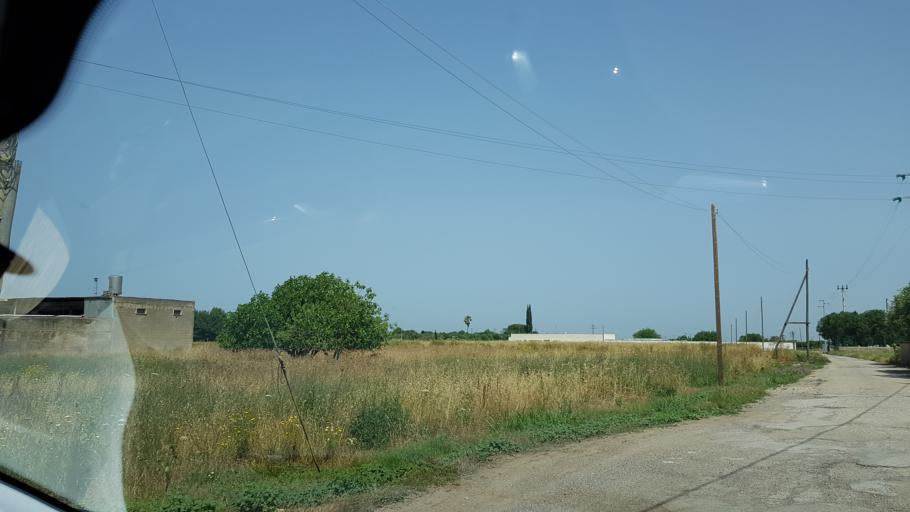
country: IT
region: Apulia
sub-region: Provincia di Brindisi
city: Mesagne
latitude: 40.5533
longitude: 17.8248
